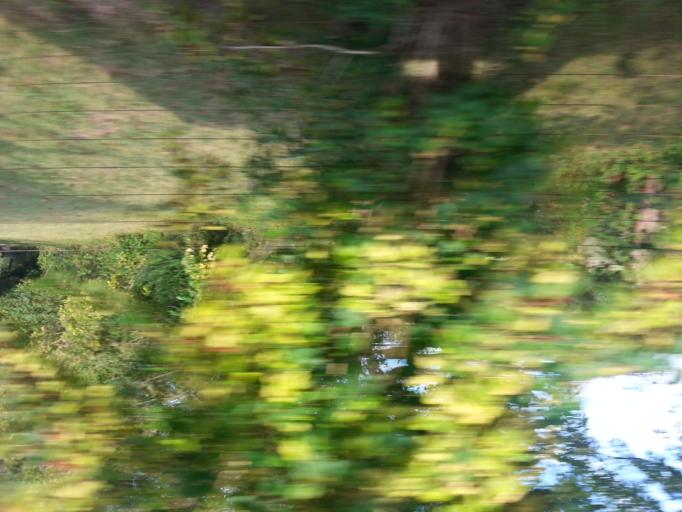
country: US
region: Tennessee
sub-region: Blount County
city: Wildwood
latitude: 35.8596
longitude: -83.8633
